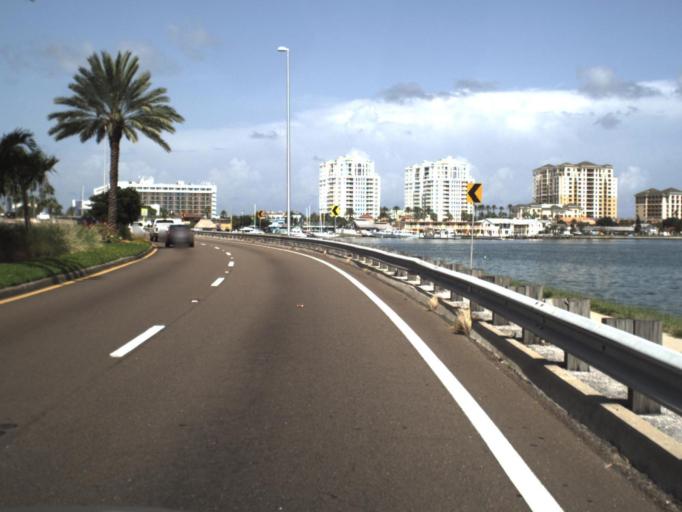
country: US
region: Florida
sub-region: Pinellas County
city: Clearwater
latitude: 27.9774
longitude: -82.8217
